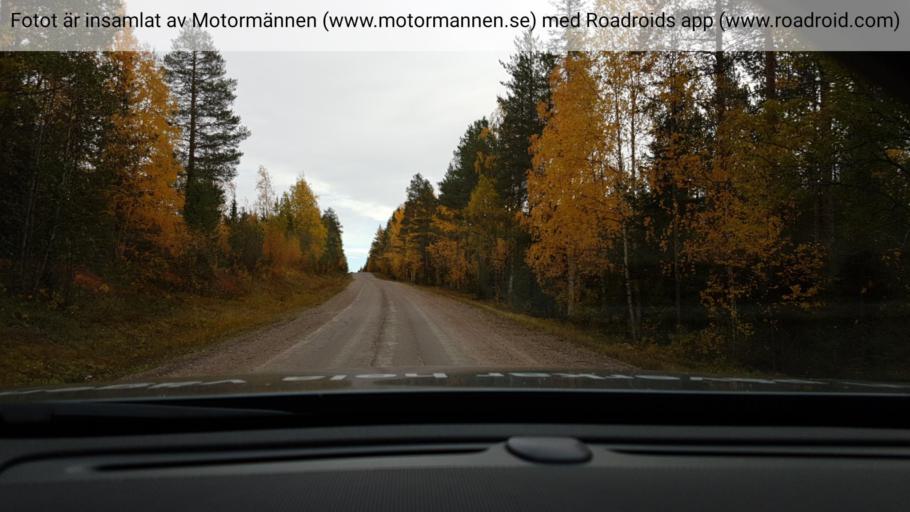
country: SE
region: Norrbotten
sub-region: Overkalix Kommun
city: OEverkalix
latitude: 66.2732
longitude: 22.9901
